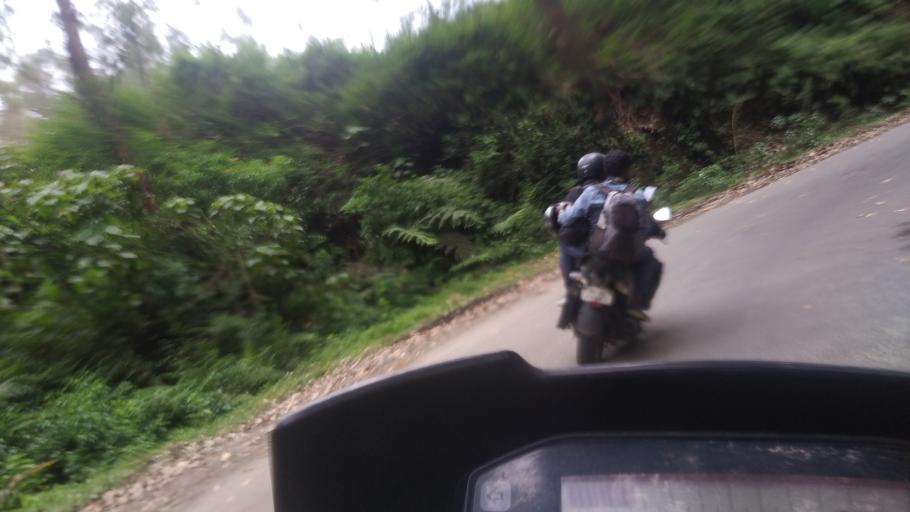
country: IN
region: Kerala
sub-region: Idukki
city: Munnar
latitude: 10.0710
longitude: 77.0987
